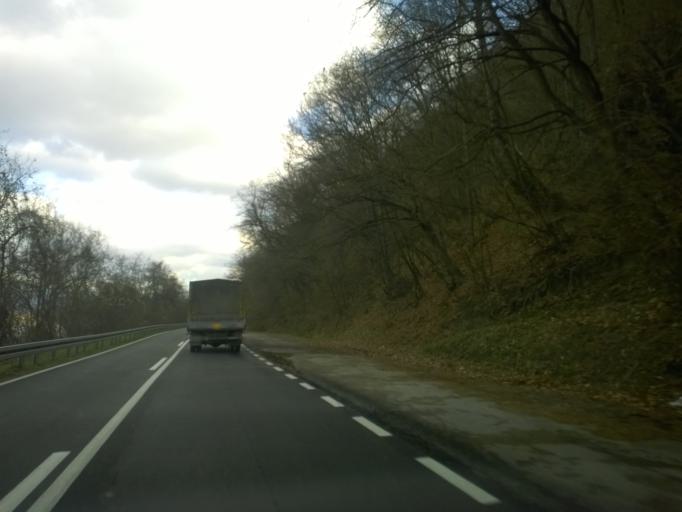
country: RO
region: Caras-Severin
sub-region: Comuna Berzasca
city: Liubcova
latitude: 44.6469
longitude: 21.8456
